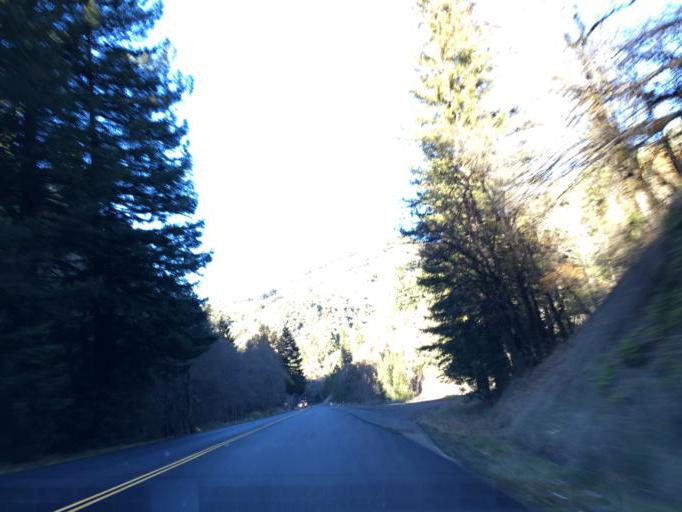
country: US
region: California
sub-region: Mendocino County
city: Laytonville
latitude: 39.8186
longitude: -123.5642
